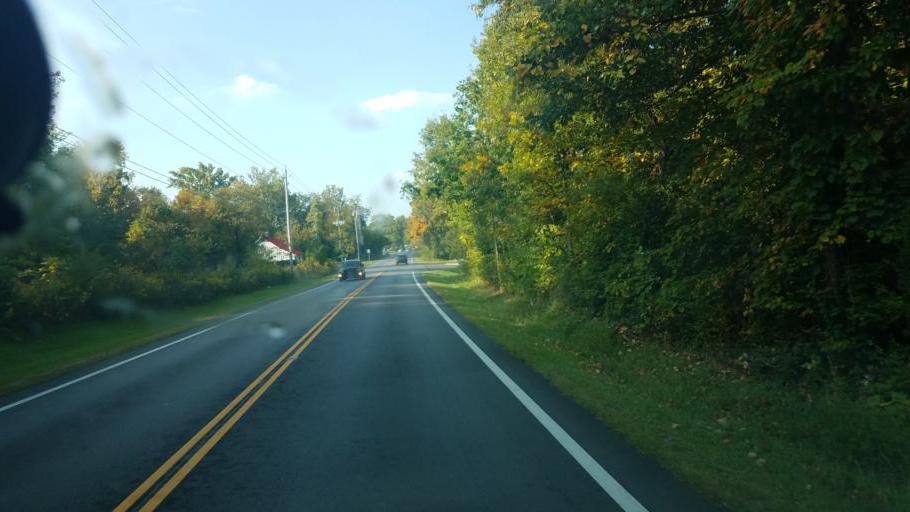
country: US
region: Ohio
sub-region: Franklin County
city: Gahanna
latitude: 40.0350
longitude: -82.8680
